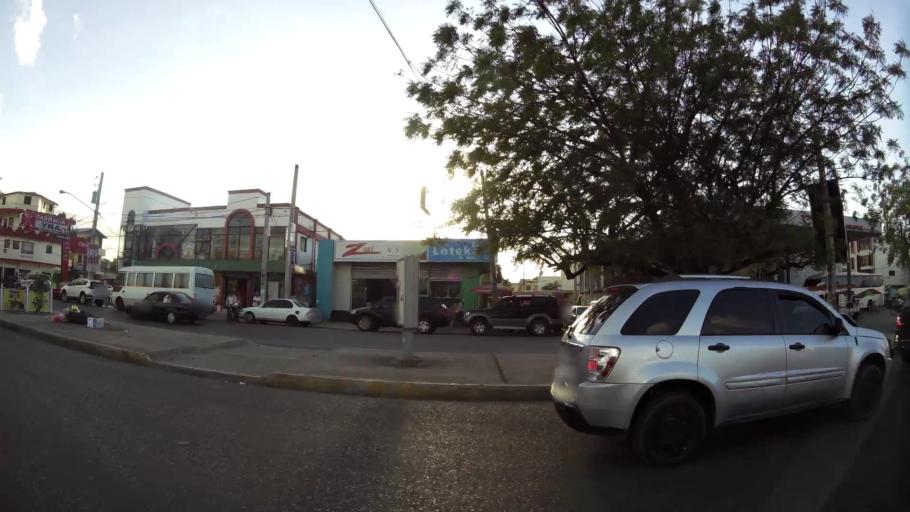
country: DO
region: Santiago
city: Santiago de los Caballeros
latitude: 19.4869
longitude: -70.7187
